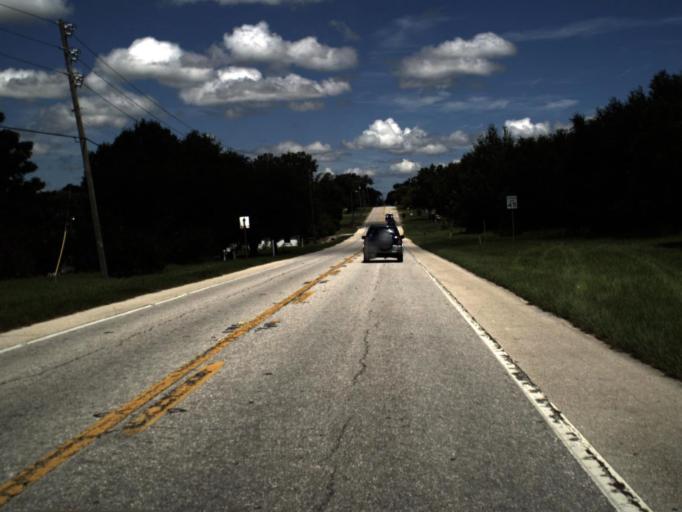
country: US
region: Florida
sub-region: Polk County
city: Lake Wales
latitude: 27.8811
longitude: -81.5814
